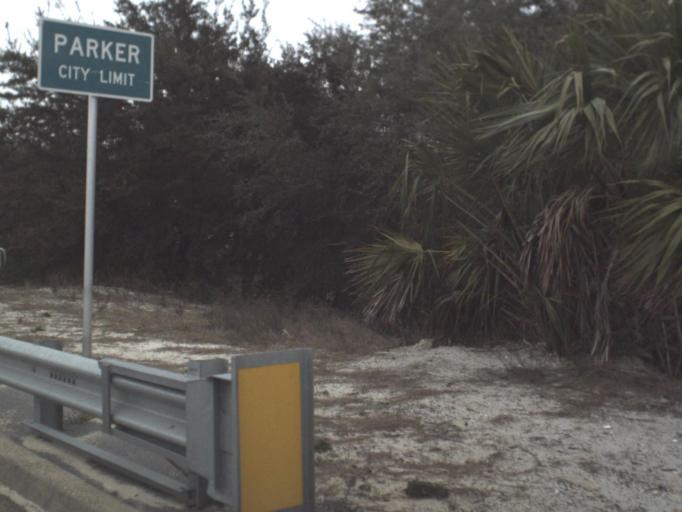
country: US
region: Florida
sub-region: Bay County
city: Tyndall Air Force Base
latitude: 30.1077
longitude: -85.6054
